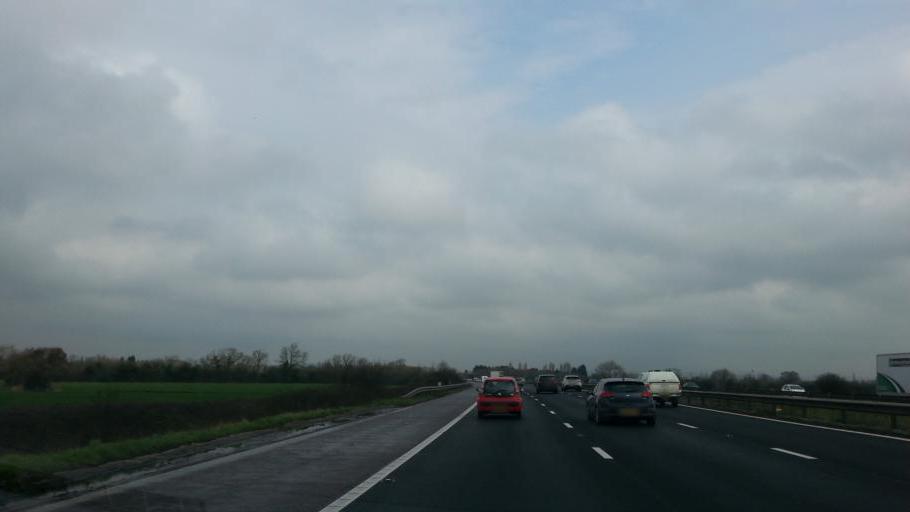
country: GB
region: England
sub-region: North Somerset
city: Kingston Seymour
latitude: 51.3918
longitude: -2.8608
